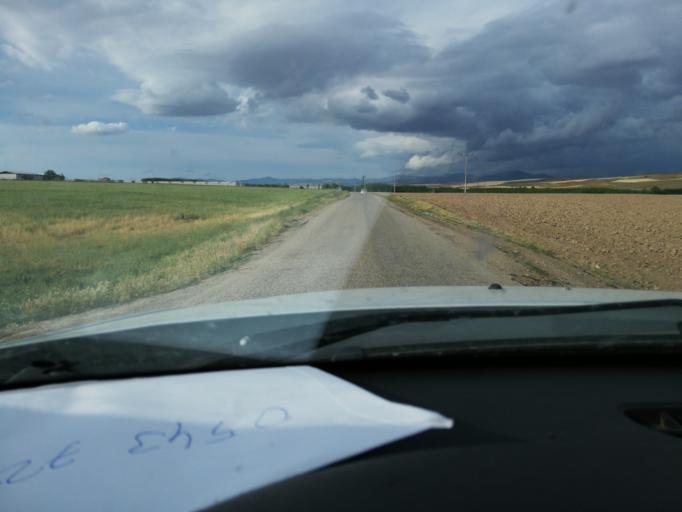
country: TR
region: Kirsehir
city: Kirsehir
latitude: 39.0166
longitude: 34.1196
